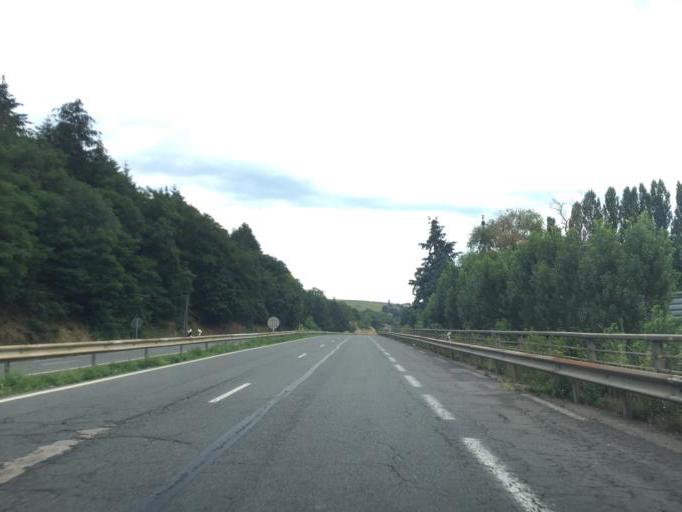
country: FR
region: Rhone-Alpes
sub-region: Departement du Rhone
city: Tarare
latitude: 45.8884
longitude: 4.4589
